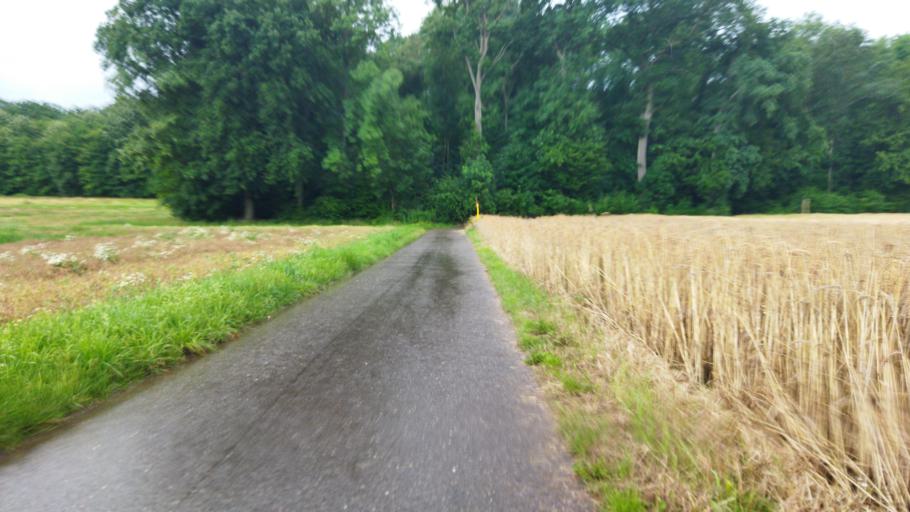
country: DE
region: Baden-Wuerttemberg
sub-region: Regierungsbezirk Stuttgart
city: Kirchardt
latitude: 49.2038
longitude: 9.0222
